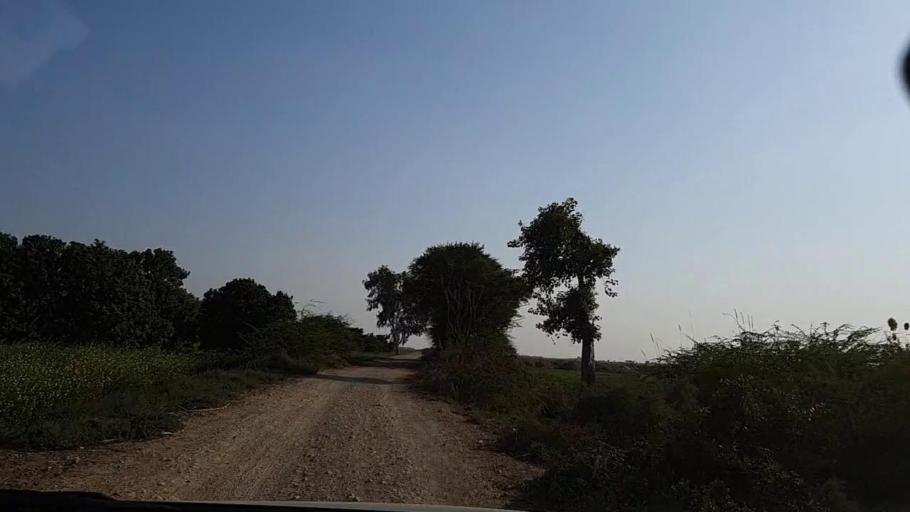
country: PK
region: Sindh
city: Mirwah Gorchani
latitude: 25.2301
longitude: 68.9731
